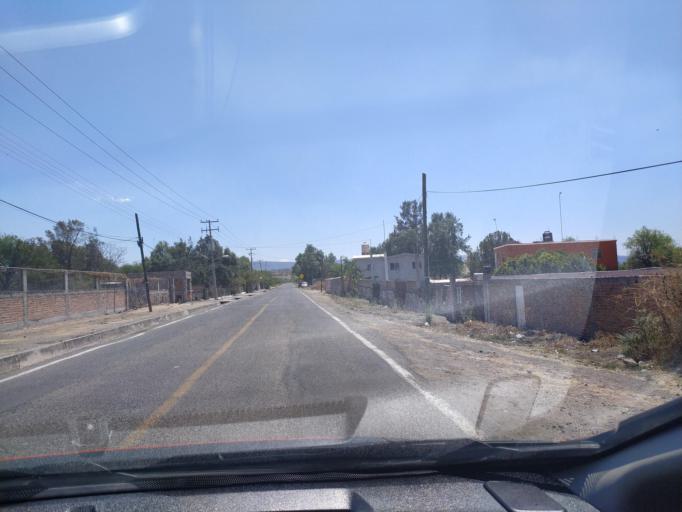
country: MX
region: Guanajuato
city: Ciudad Manuel Doblado
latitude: 20.7487
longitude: -101.8245
